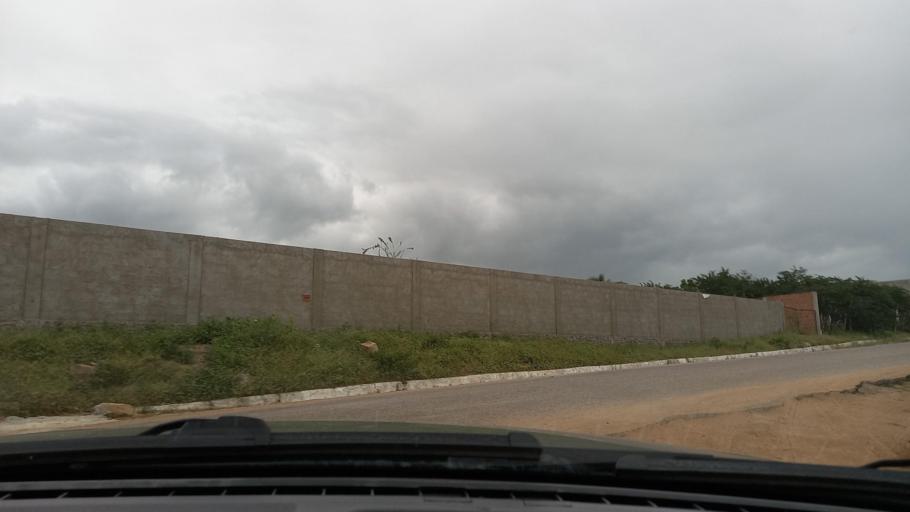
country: BR
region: Sergipe
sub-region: Caninde De Sao Francisco
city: Caninde de Sao Francisco
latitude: -9.6151
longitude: -37.7621
